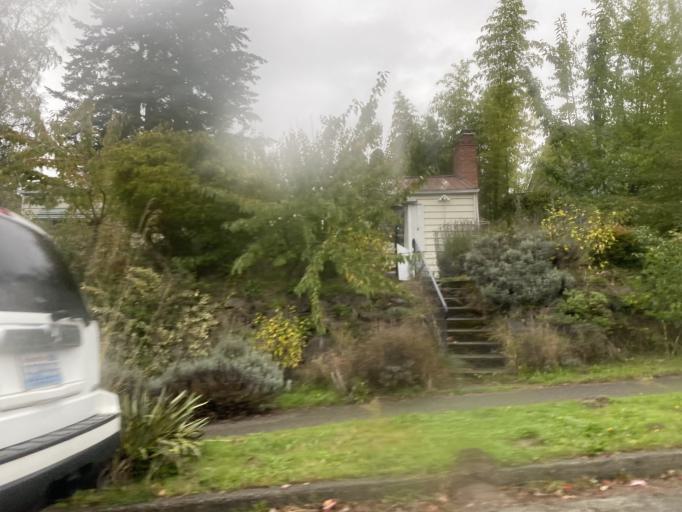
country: US
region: Washington
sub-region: King County
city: Seattle
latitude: 47.6533
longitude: -122.4068
